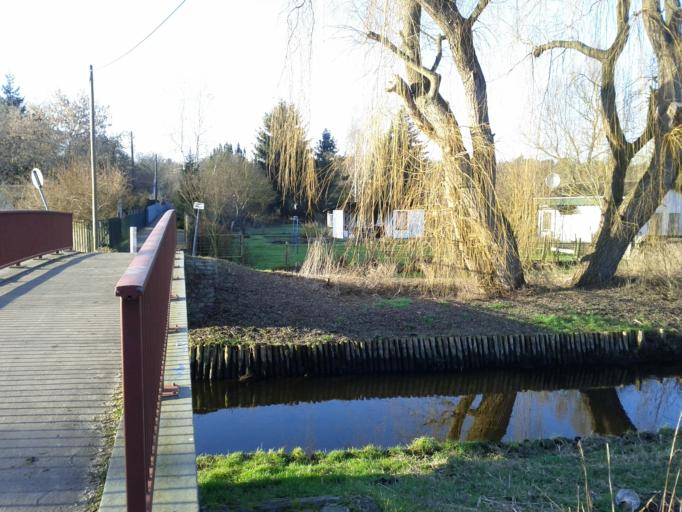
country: DE
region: Berlin
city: Friedrichshagen
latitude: 52.4600
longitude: 13.6206
